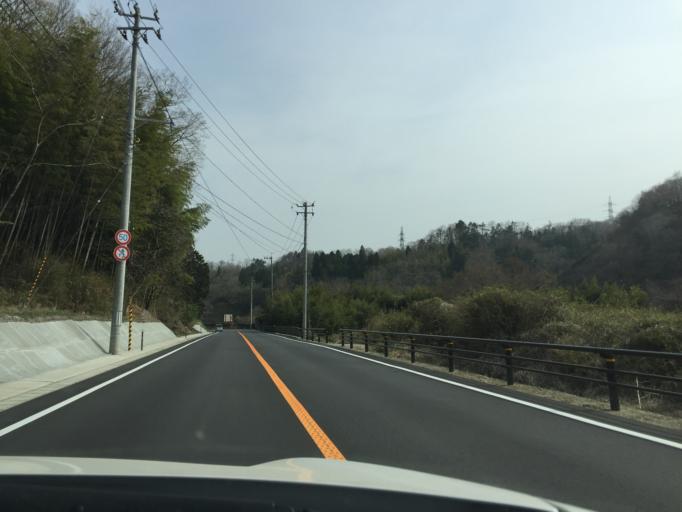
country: JP
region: Fukushima
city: Iwaki
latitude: 37.0106
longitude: 140.7776
